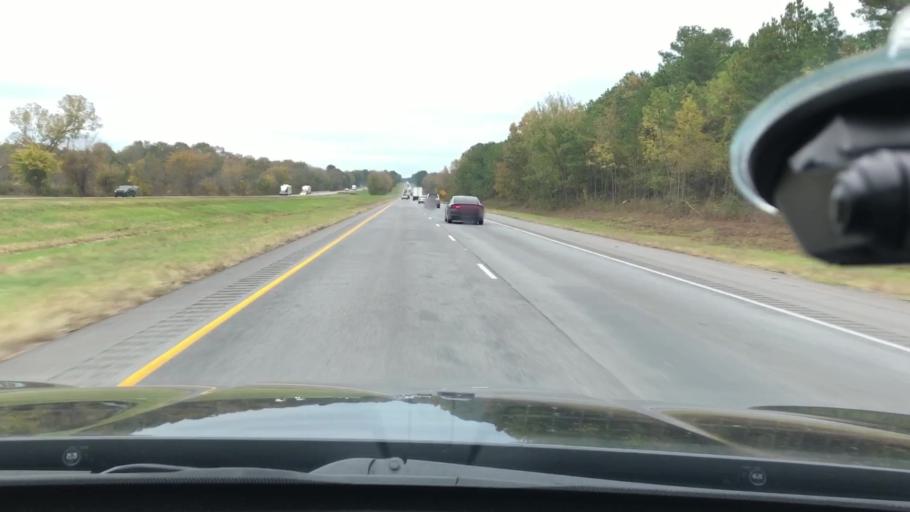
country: US
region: Arkansas
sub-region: Hempstead County
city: Hope
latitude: 33.6238
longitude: -93.7661
